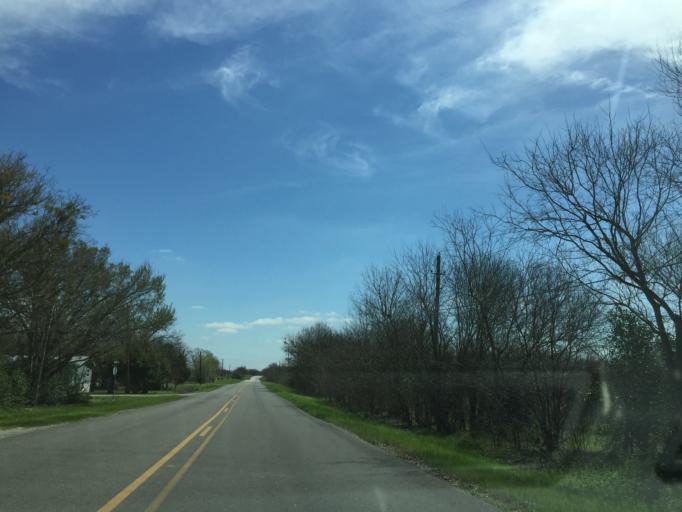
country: US
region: Texas
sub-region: Williamson County
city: Taylor
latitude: 30.5648
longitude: -97.3967
